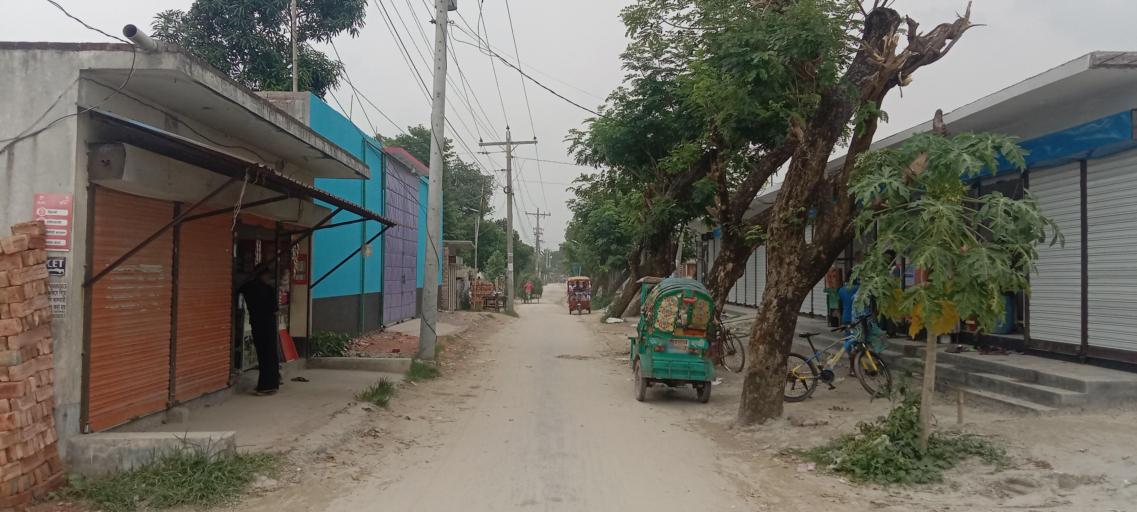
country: BD
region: Dhaka
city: Azimpur
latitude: 23.7061
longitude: 90.3505
